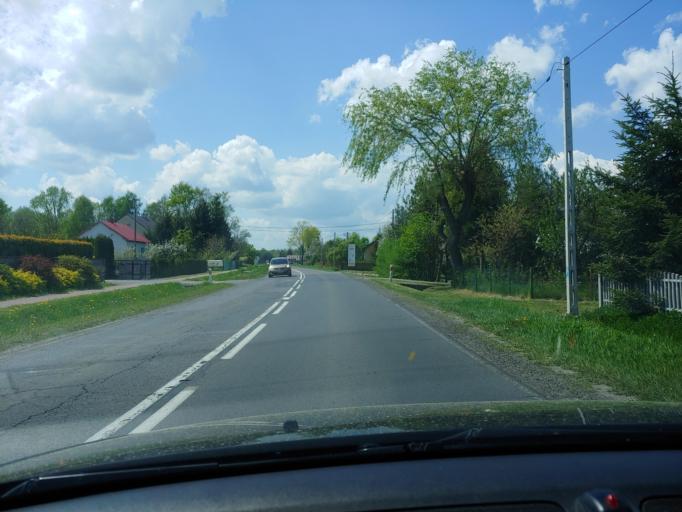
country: PL
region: Subcarpathian Voivodeship
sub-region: Powiat mielecki
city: Wadowice Gorne
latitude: 50.2595
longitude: 21.3340
